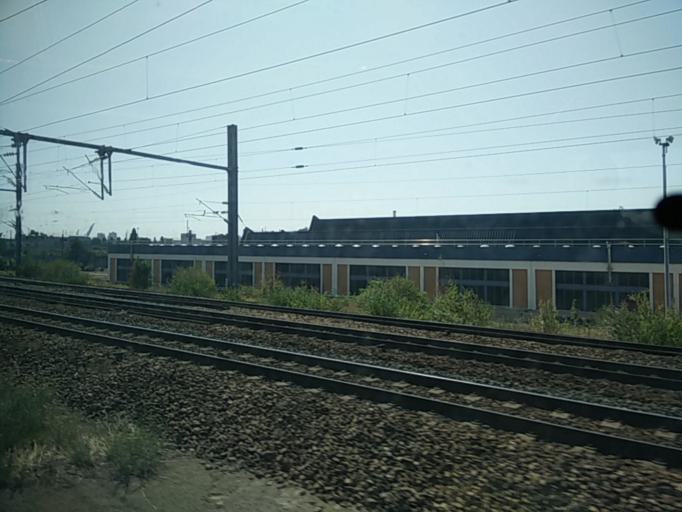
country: FR
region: Ile-de-France
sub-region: Departement de Seine-Saint-Denis
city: Romainville
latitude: 48.8990
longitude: 2.4301
